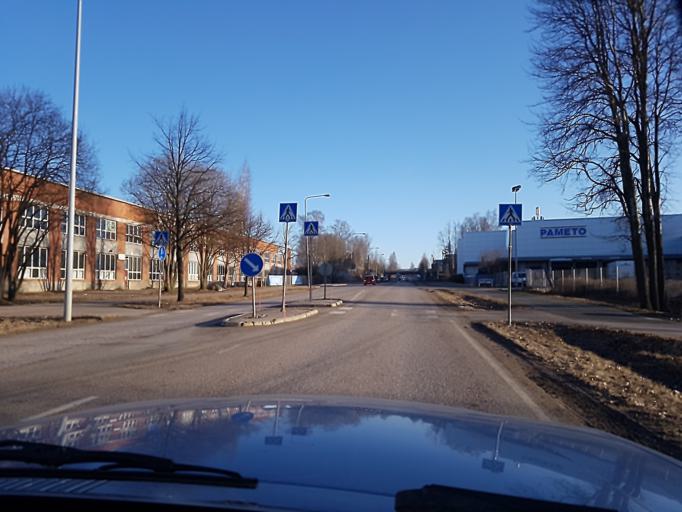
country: FI
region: Uusimaa
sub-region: Helsinki
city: Vantaa
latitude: 60.2982
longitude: 24.9854
